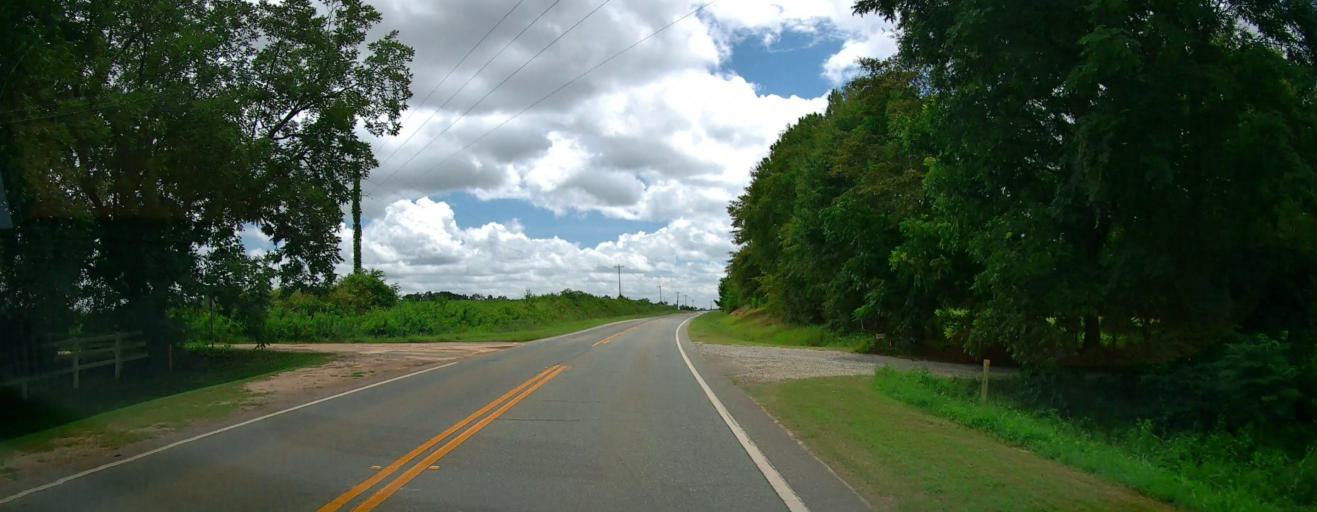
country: US
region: Georgia
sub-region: Wilcox County
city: Rochelle
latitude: 31.9882
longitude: -83.5455
